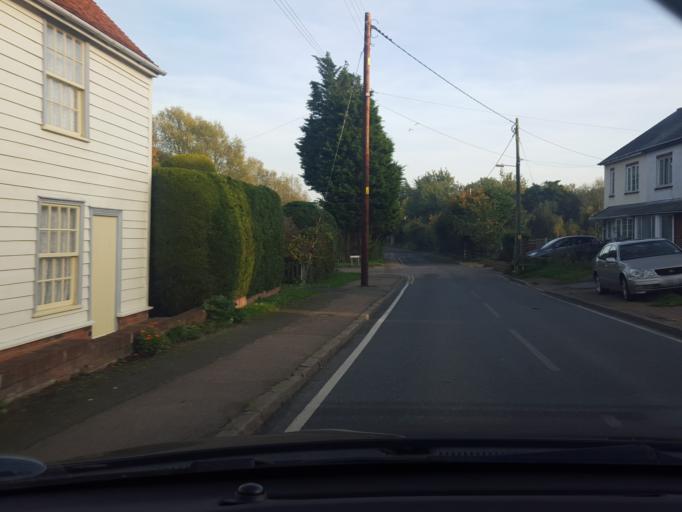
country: GB
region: England
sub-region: Essex
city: Saint Osyth
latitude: 51.7968
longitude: 1.0810
